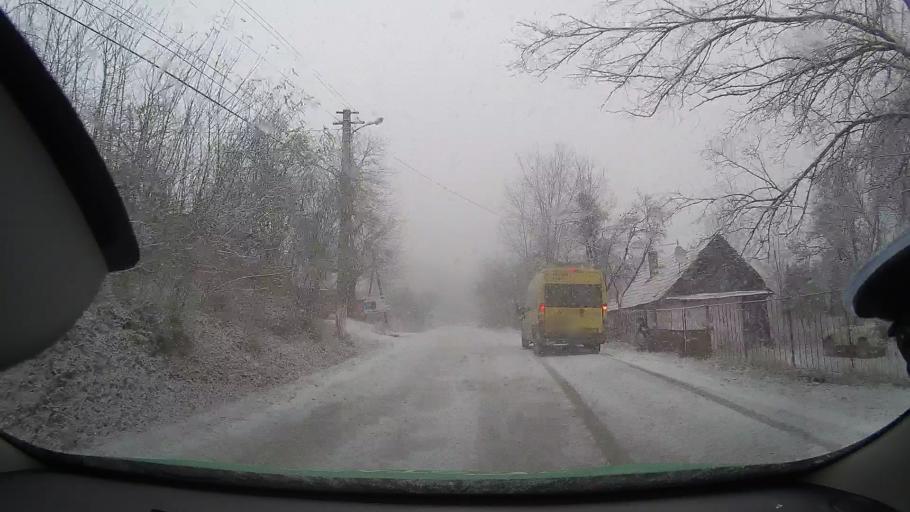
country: RO
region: Alba
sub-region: Comuna Hoparta
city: Hoparta
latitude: 46.3231
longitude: 23.8753
